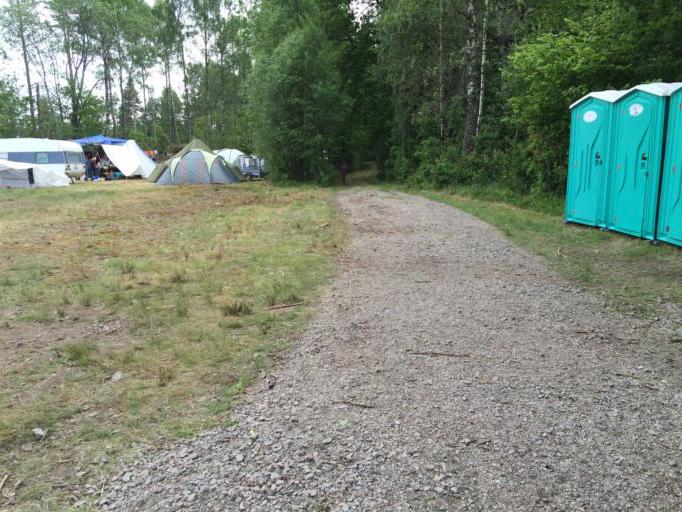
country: SE
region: Vaestra Goetaland
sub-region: Fargelanda Kommun
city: Faergelanda
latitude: 58.5829
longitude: 12.0851
